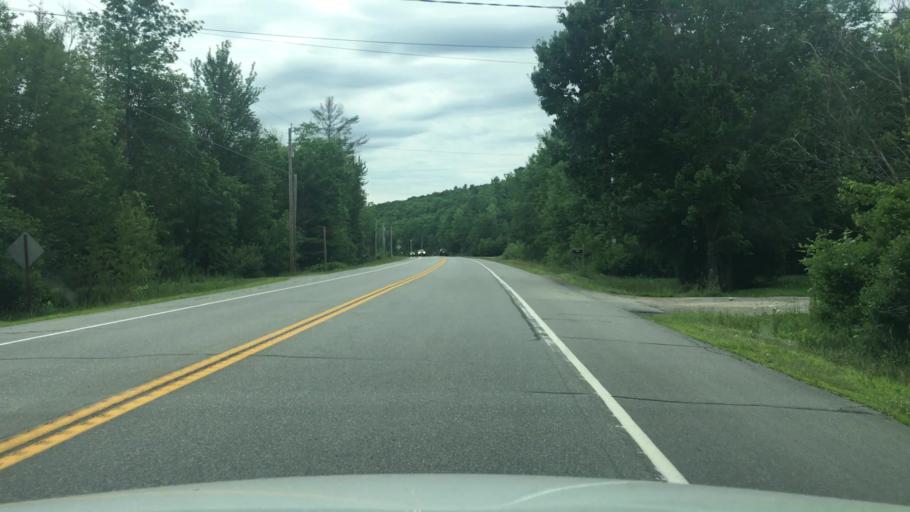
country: US
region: Maine
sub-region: Kennebec County
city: Windsor
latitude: 44.3743
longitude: -69.6270
